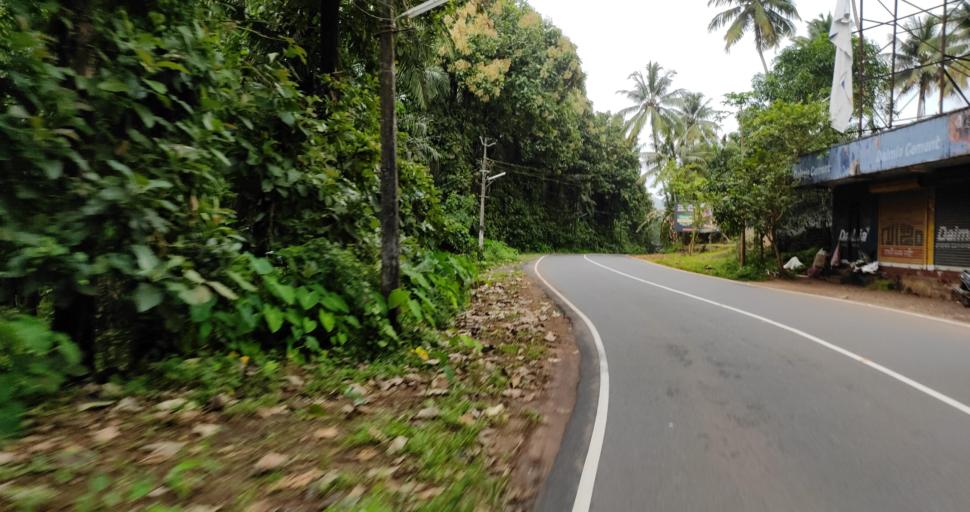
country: IN
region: Kerala
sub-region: Ernakulam
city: Angamali
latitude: 10.2938
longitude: 76.4949
